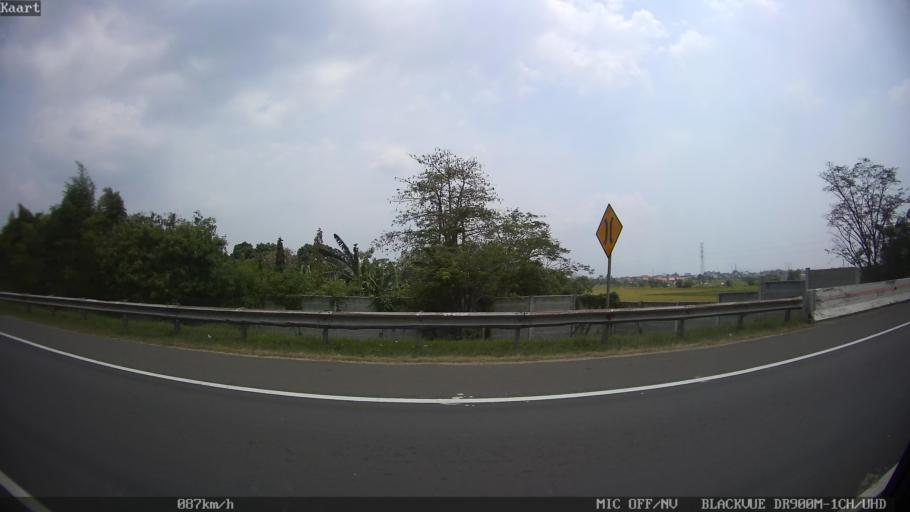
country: ID
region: Banten
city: Bojonegara
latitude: -6.0111
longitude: 106.0757
